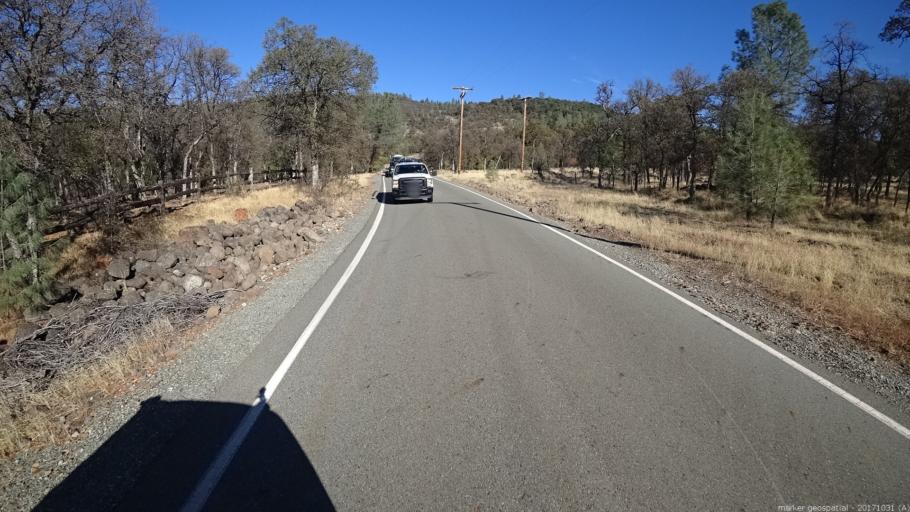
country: US
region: California
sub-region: Shasta County
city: Shingletown
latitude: 40.4548
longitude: -121.8994
